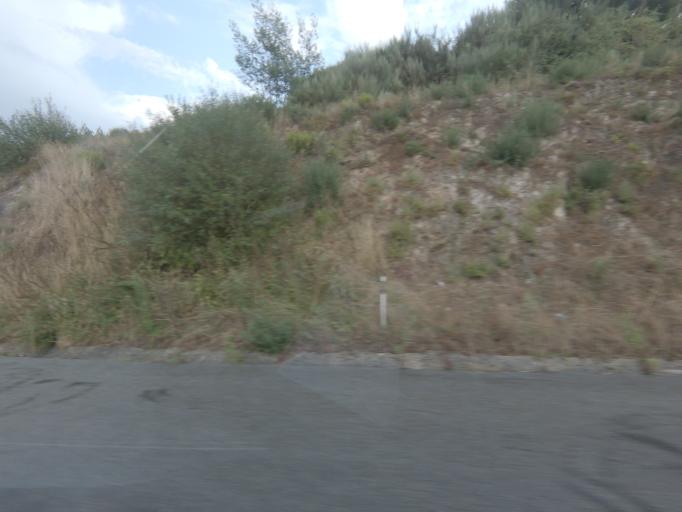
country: PT
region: Viseu
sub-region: Castro Daire
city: Castro Daire
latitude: 40.8789
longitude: -7.9201
